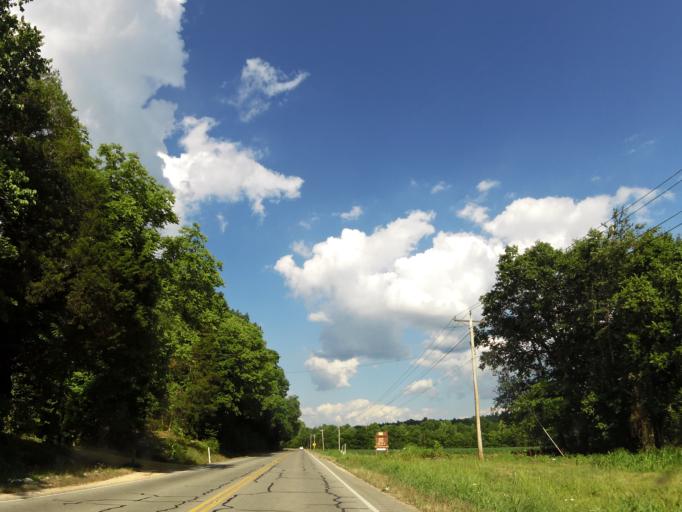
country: US
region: Tennessee
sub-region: Perry County
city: Linden
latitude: 35.6350
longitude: -87.8013
